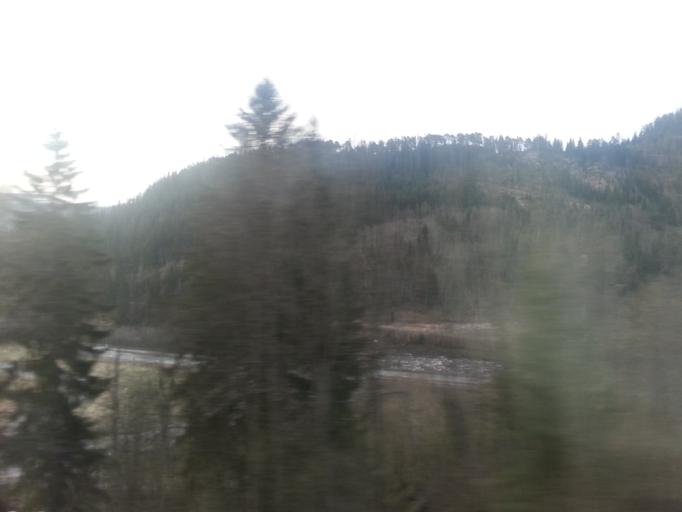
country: NO
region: Sor-Trondelag
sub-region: Midtre Gauldal
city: Storen
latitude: 63.0263
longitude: 10.2520
